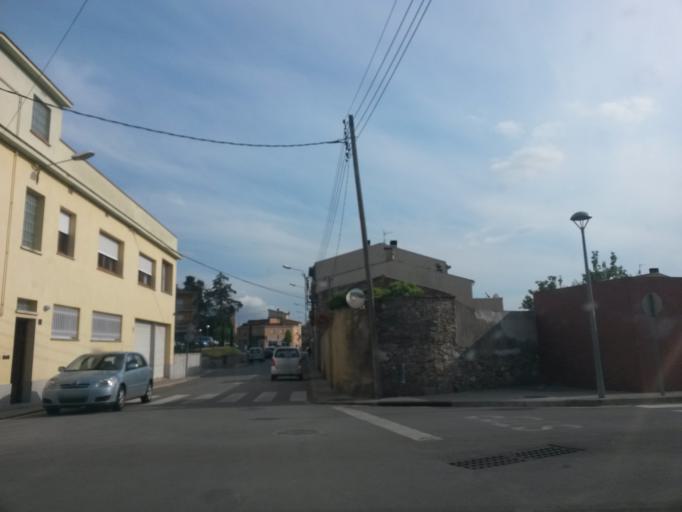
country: ES
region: Catalonia
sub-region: Provincia de Girona
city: Caldes de Malavella
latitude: 41.8406
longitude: 2.8098
